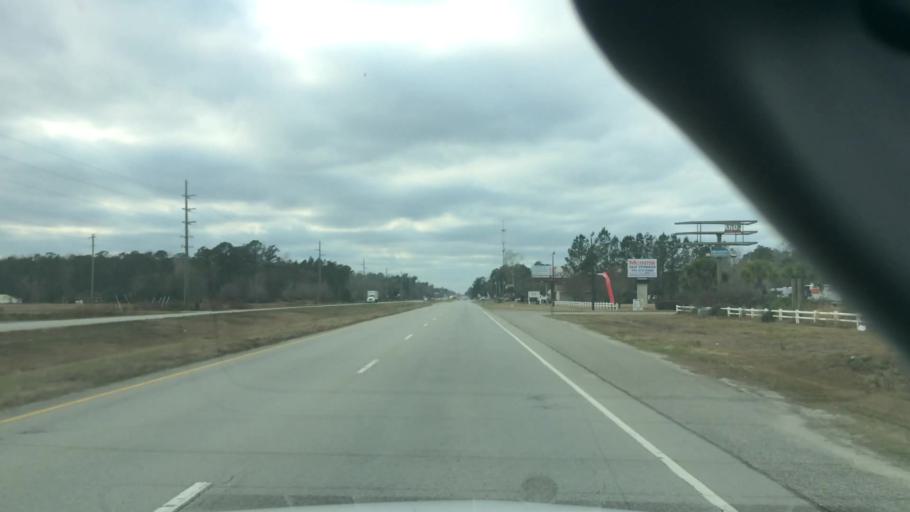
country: US
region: North Carolina
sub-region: Brunswick County
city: Sunset Beach
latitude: 33.9498
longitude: -78.4805
